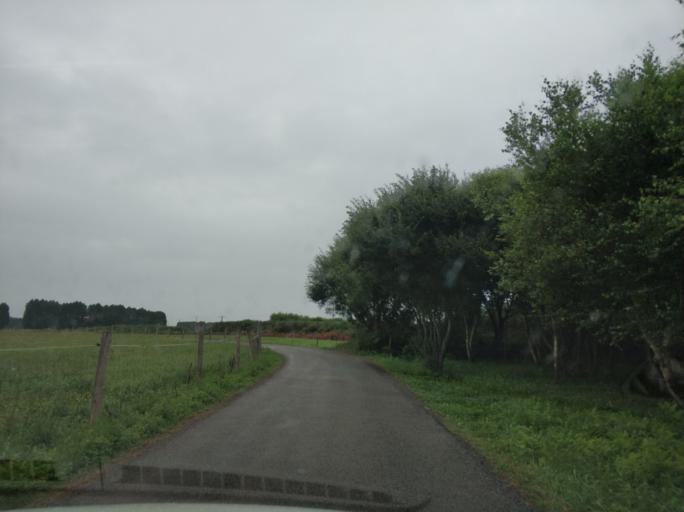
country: ES
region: Asturias
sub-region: Province of Asturias
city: Tineo
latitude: 43.5607
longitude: -6.4679
